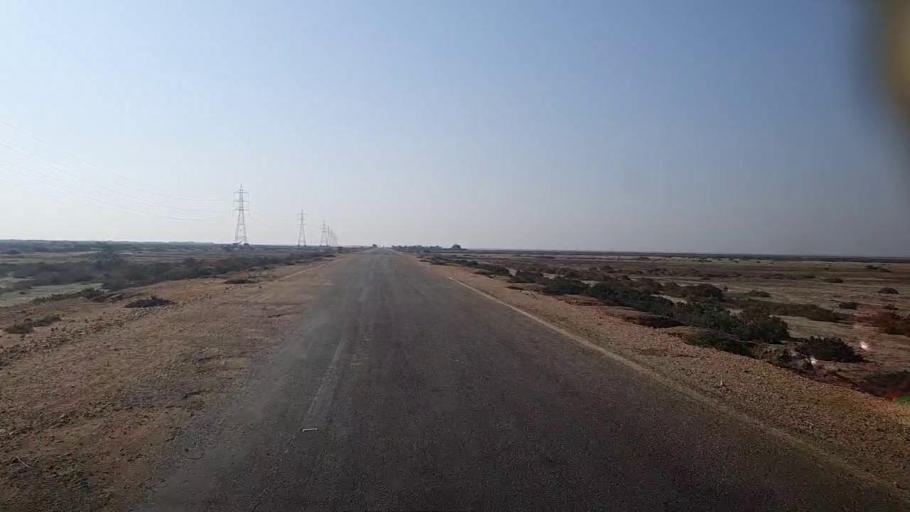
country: PK
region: Sindh
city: Gharo
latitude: 24.6212
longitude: 67.4969
